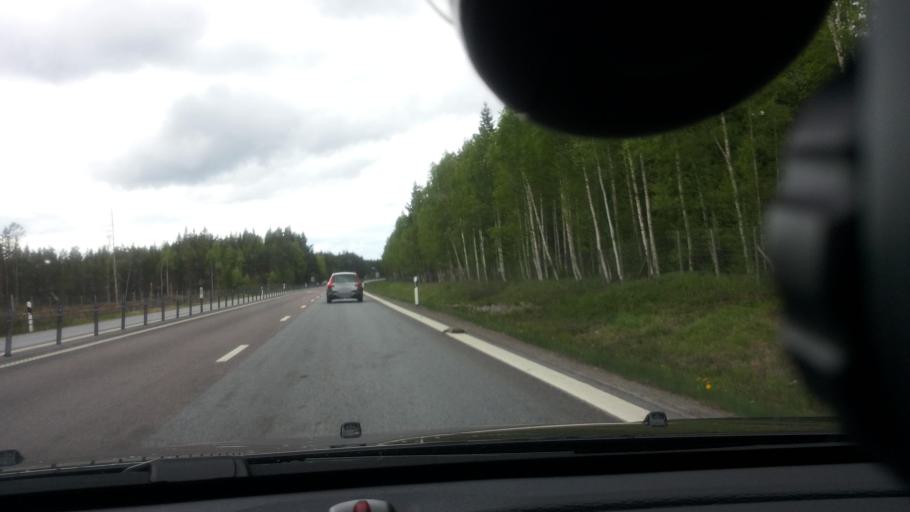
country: SE
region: Gaevleborg
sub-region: Gavle Kommun
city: Norrsundet
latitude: 60.8676
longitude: 17.0557
